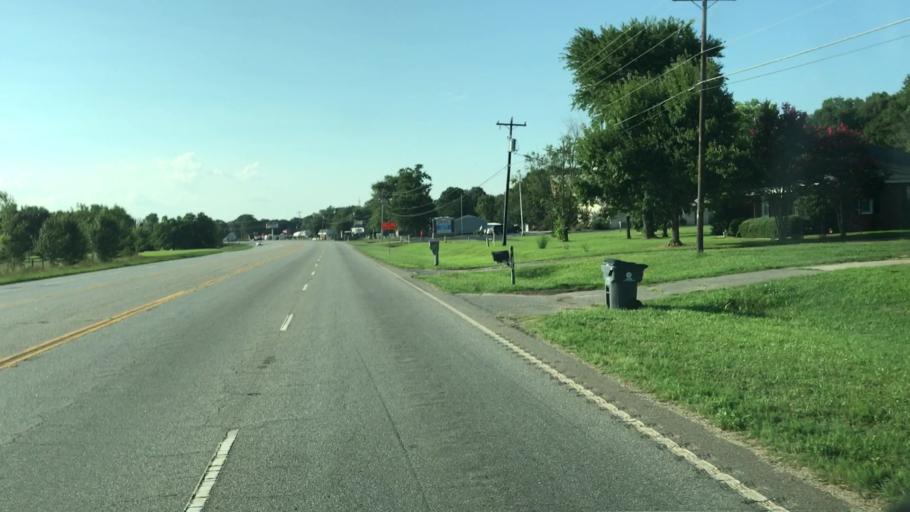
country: US
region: South Carolina
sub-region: Anderson County
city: Piedmont
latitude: 34.6628
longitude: -82.3931
